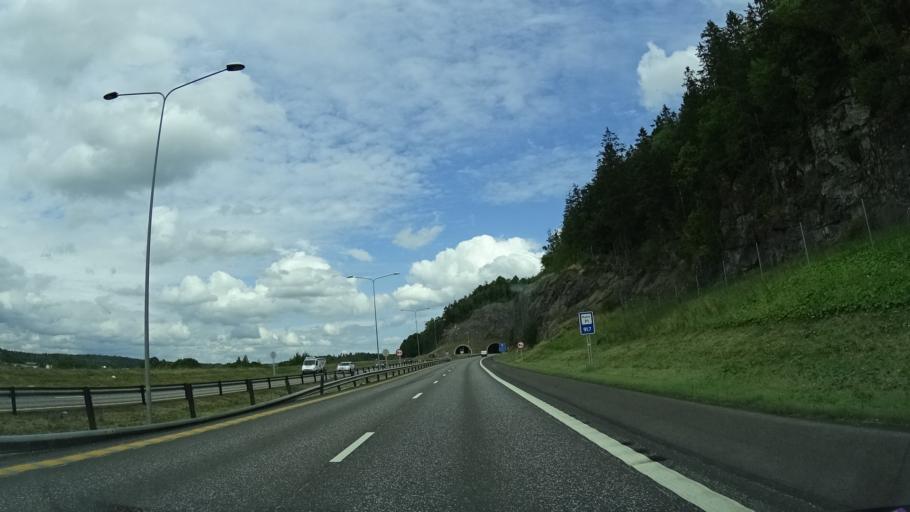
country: NO
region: Vestfold
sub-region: Tonsberg
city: Barkaker
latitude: 59.3417
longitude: 10.3801
